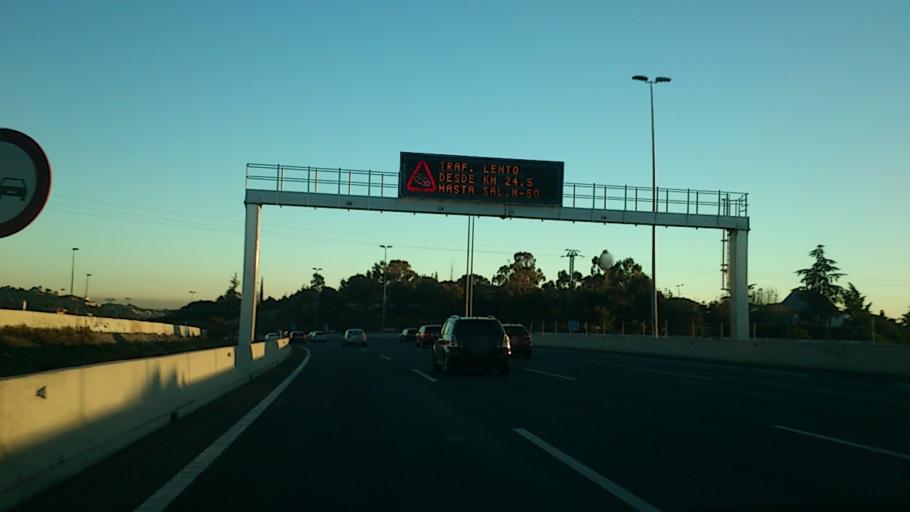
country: ES
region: Madrid
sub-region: Provincia de Madrid
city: Torrelodones
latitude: 40.5998
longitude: -3.9631
